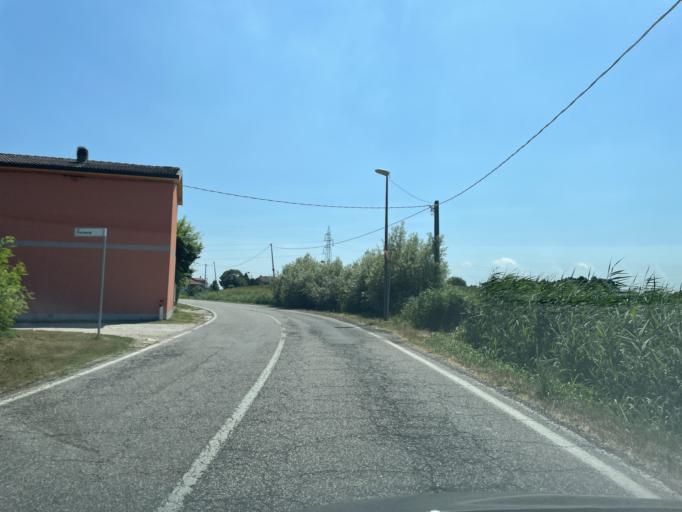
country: IT
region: Veneto
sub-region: Provincia di Verona
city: San Martino Buon Albergo
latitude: 45.3961
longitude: 11.0839
